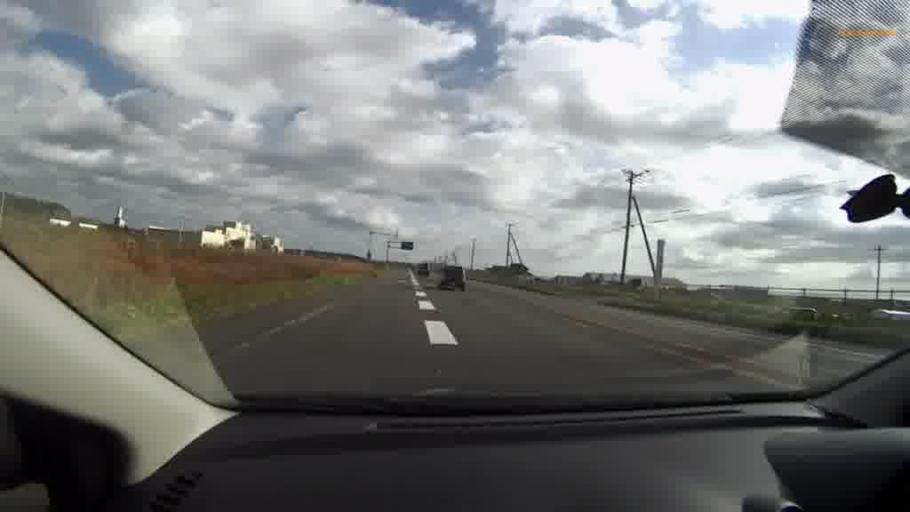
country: JP
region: Hokkaido
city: Kushiro
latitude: 42.9686
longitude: 144.1205
